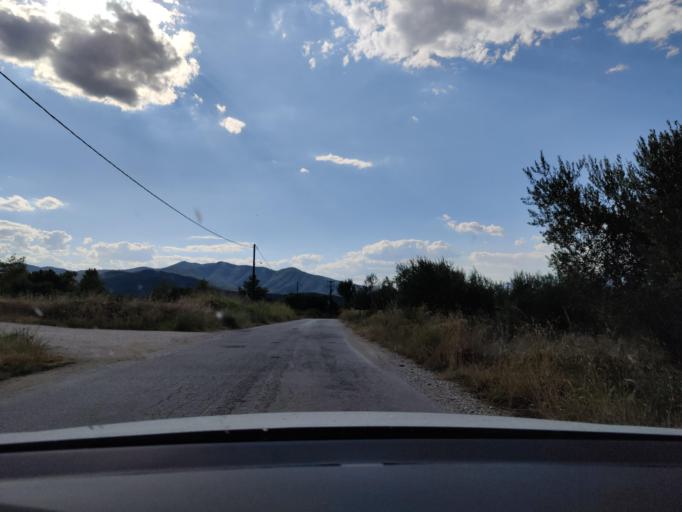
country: GR
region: Central Macedonia
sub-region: Nomos Serron
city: Chrysochorafa
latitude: 41.1764
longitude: 23.1166
